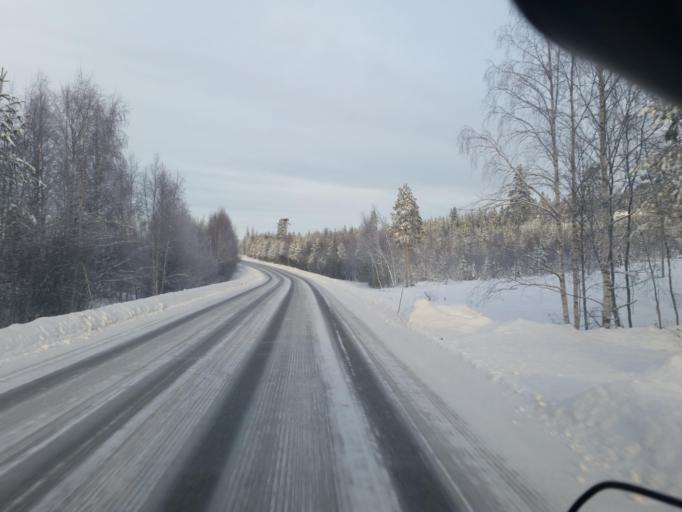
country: SE
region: Norrbotten
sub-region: Pitea Kommun
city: Norrfjarden
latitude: 65.4492
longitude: 21.4567
